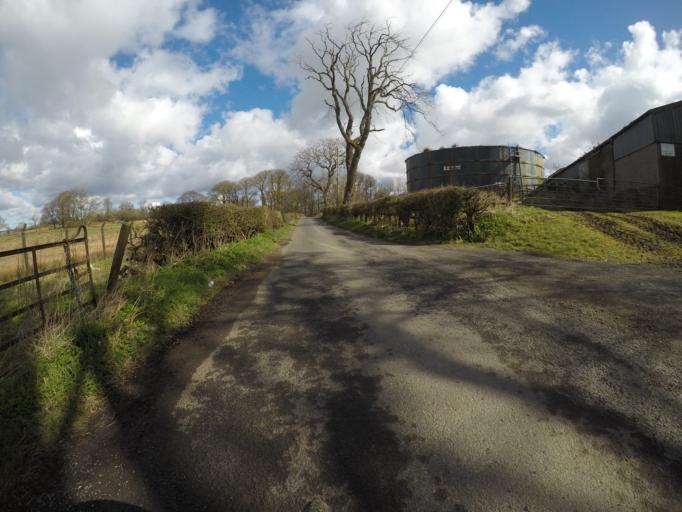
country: GB
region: Scotland
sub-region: North Ayrshire
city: Beith
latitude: 55.7282
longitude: -4.6072
